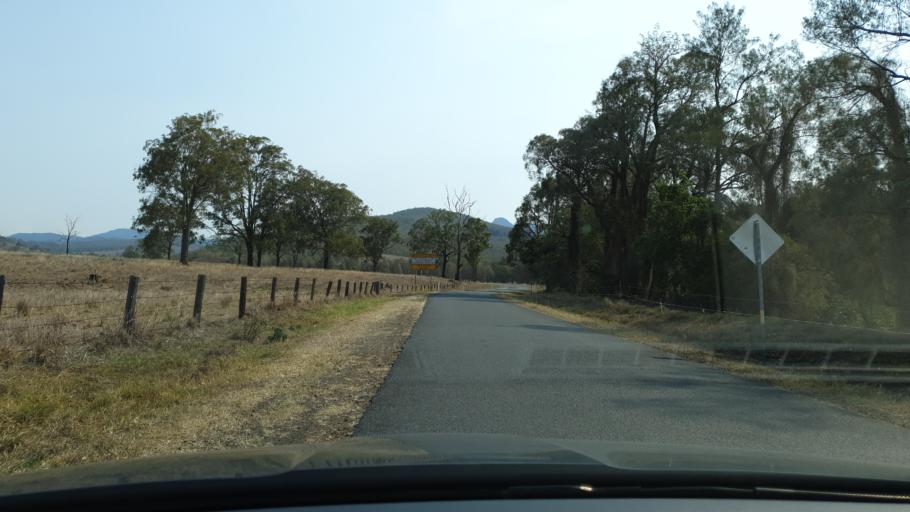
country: AU
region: Queensland
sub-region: Southern Downs
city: Warwick
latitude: -28.1836
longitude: 152.5457
